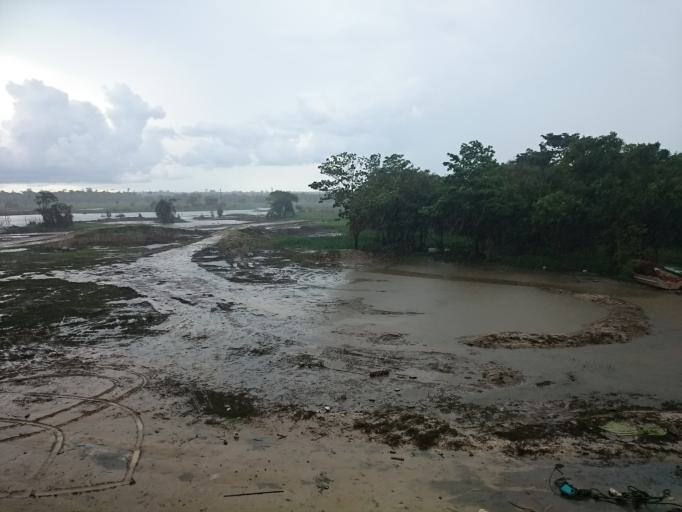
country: PE
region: Loreto
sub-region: Provincia de Maynas
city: Iquitos
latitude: -3.7014
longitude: -73.2524
